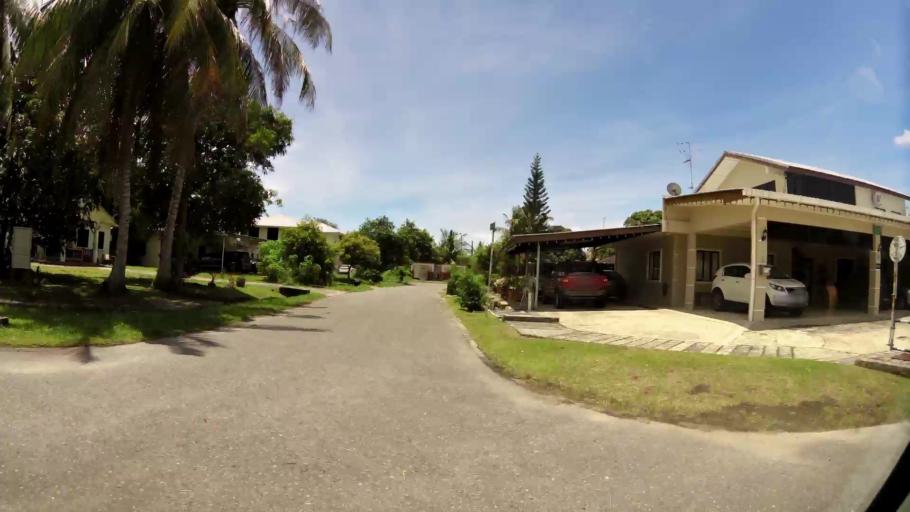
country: BN
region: Belait
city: Kuala Belait
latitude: 4.5845
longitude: 114.2403
